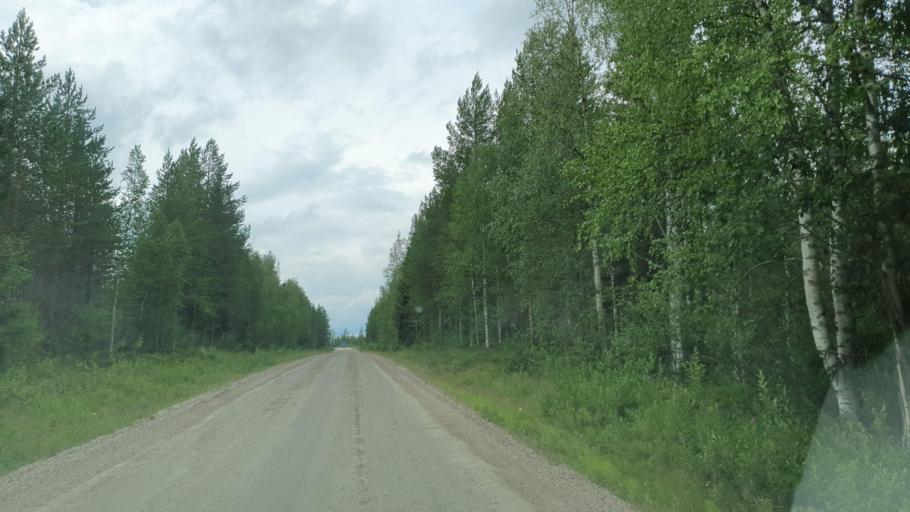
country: FI
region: Kainuu
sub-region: Kehys-Kainuu
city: Kuhmo
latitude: 64.7239
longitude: 29.6747
